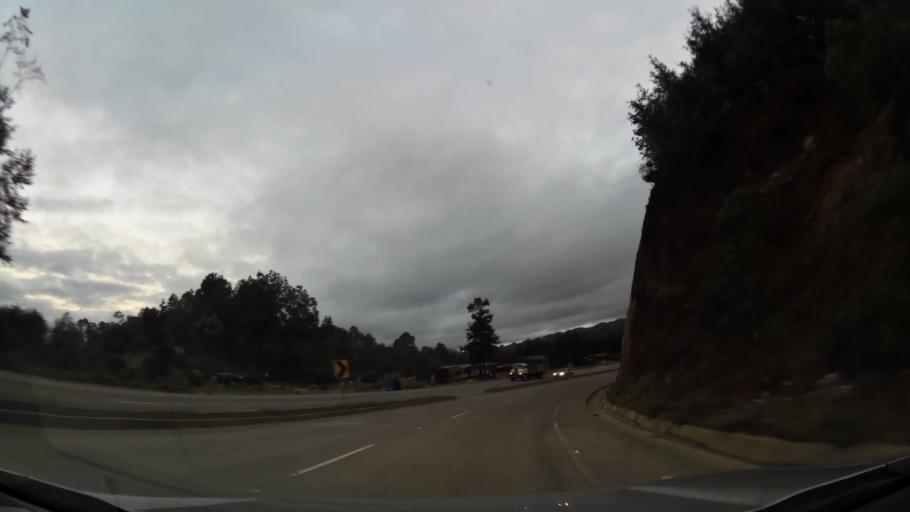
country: GT
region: Quiche
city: Chichicastenango
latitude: 14.8554
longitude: -91.0508
